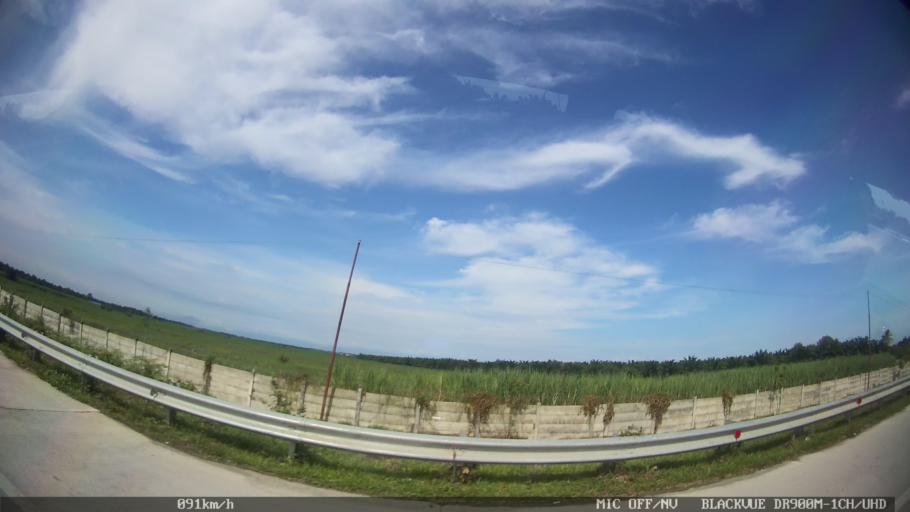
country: ID
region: North Sumatra
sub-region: Kabupaten Langkat
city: Stabat
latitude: 3.7255
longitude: 98.4922
